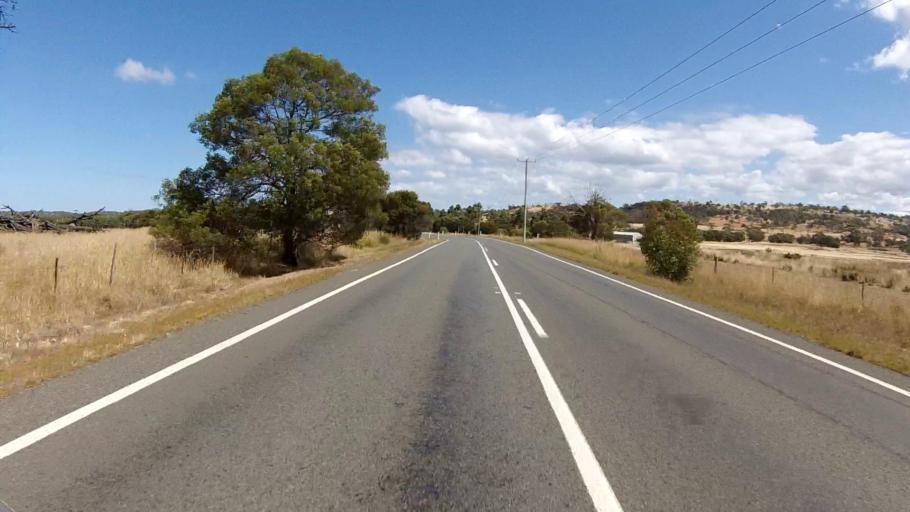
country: AU
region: Tasmania
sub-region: Break O'Day
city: St Helens
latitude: -42.1047
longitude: 148.0581
